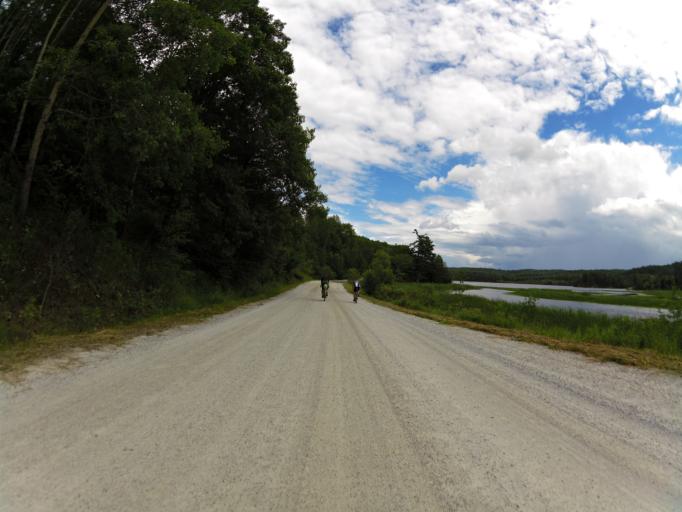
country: CA
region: Ontario
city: Renfrew
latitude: 45.1359
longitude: -76.6482
